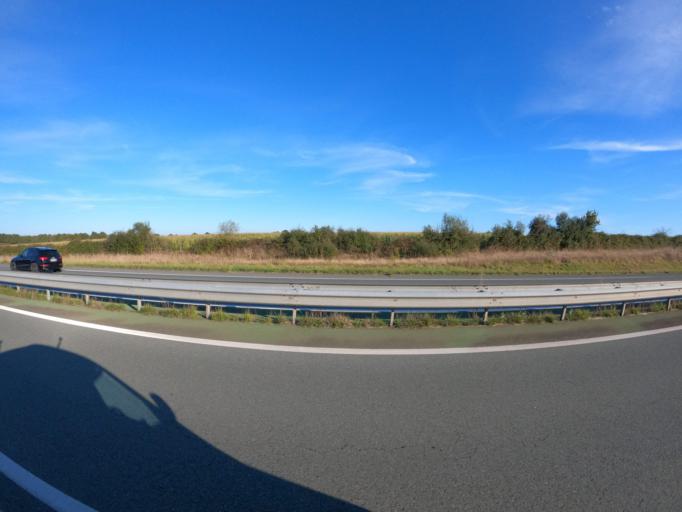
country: FR
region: Pays de la Loire
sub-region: Departement de Maine-et-Loire
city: Trementines
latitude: 47.1842
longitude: -0.7799
